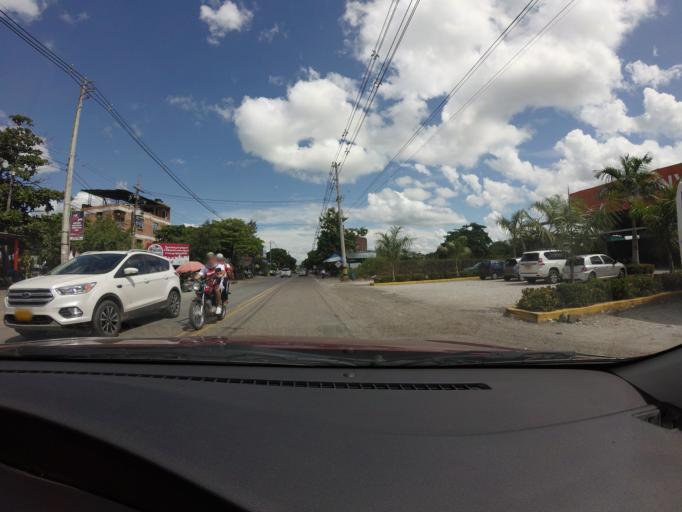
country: CO
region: Antioquia
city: Puerto Triunfo
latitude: 5.8983
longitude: -74.7368
